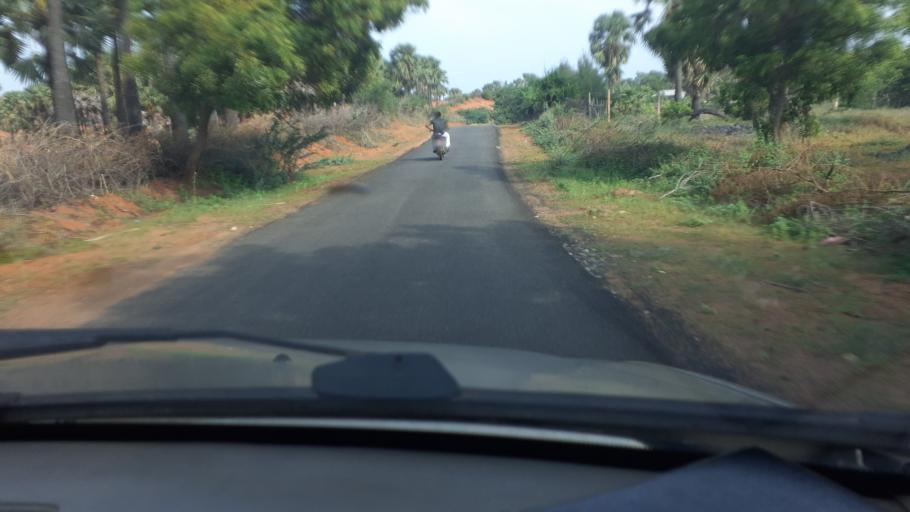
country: IN
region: Tamil Nadu
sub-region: Tirunelveli Kattabo
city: Tisaiyanvilai
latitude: 8.3376
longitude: 77.9458
